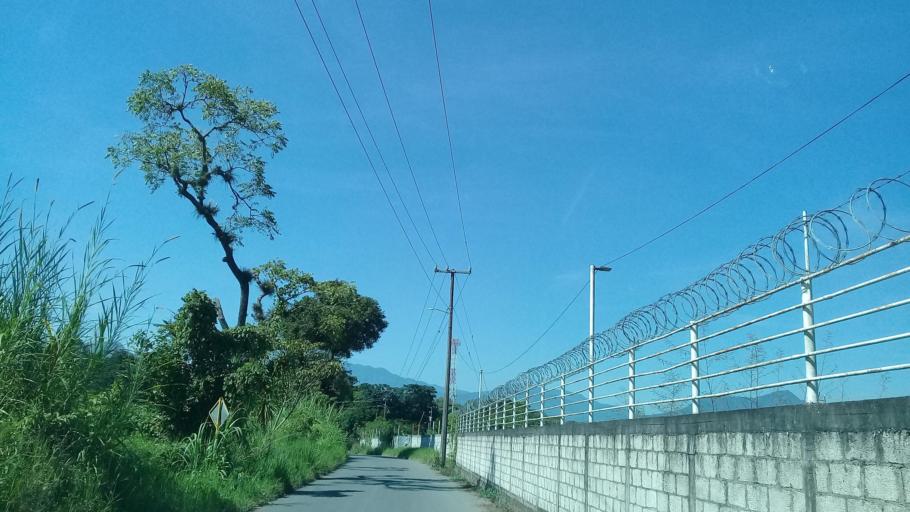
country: MX
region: Veracruz
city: Amatlan de los Reyes
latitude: 18.8549
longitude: -96.9089
